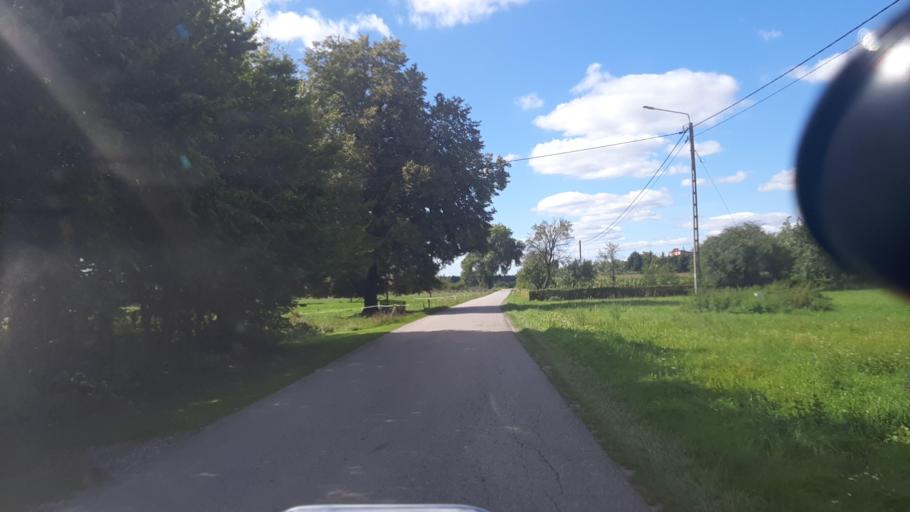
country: PL
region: Lublin Voivodeship
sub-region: Powiat lubelski
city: Garbow
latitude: 51.4066
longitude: 22.4007
